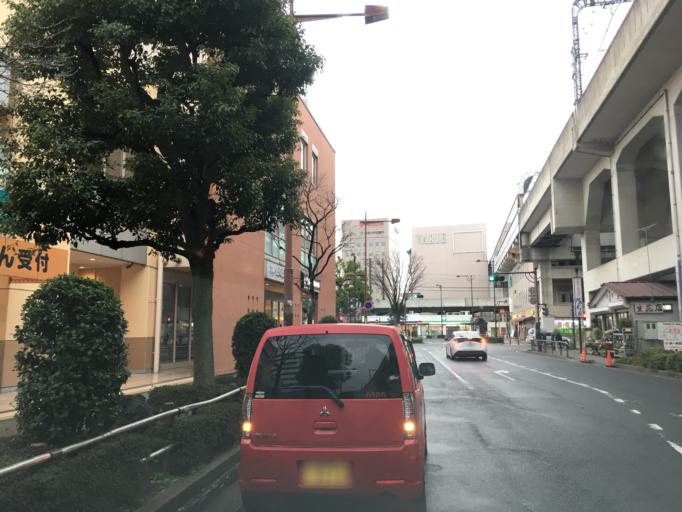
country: JP
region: Saitama
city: Koshigaya
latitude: 35.8772
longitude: 139.7898
